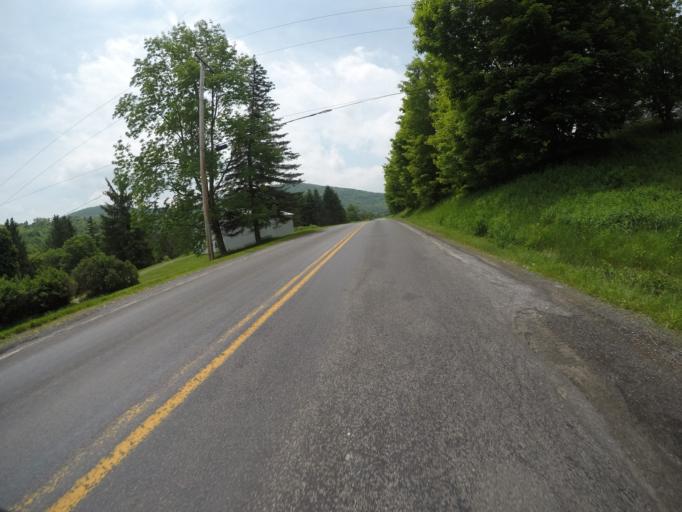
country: US
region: New York
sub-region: Delaware County
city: Delhi
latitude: 42.2636
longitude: -74.7614
